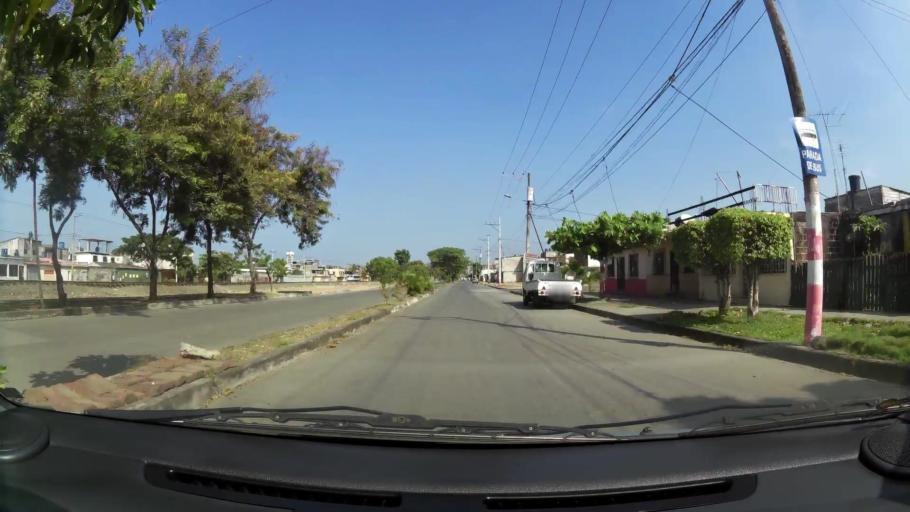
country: EC
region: Guayas
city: Eloy Alfaro
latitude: -2.1703
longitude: -79.8009
